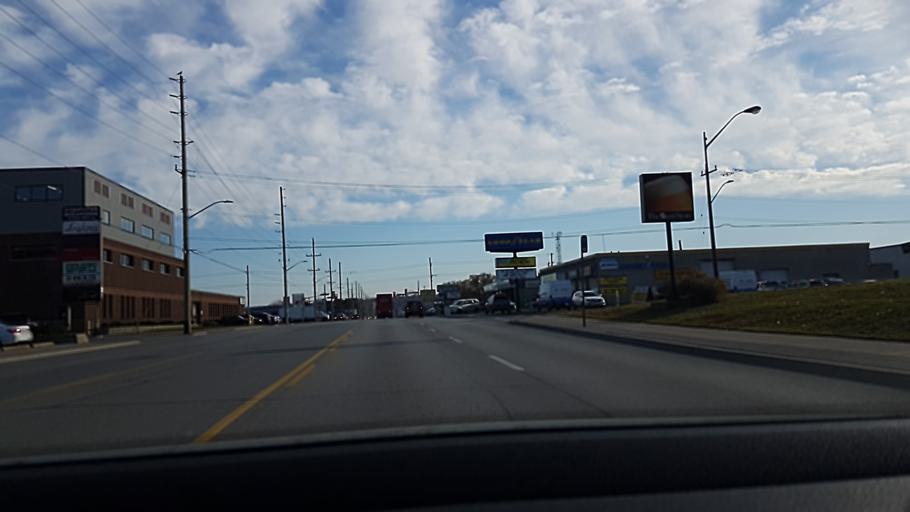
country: CA
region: Ontario
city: Barrie
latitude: 44.3812
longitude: -79.7041
